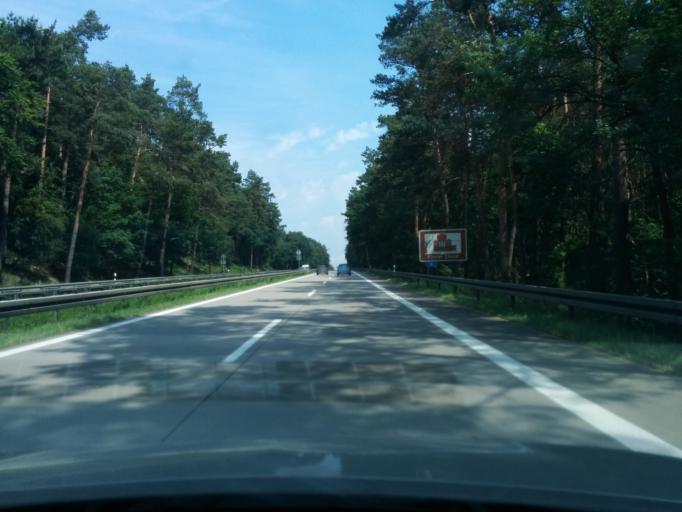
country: DE
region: Brandenburg
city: Britz
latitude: 52.9064
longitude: 13.7439
